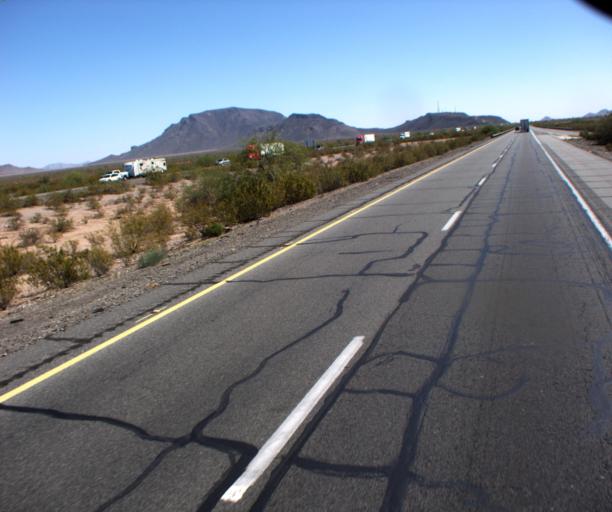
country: US
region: Arizona
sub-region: La Paz County
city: Salome
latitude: 33.5365
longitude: -113.1517
